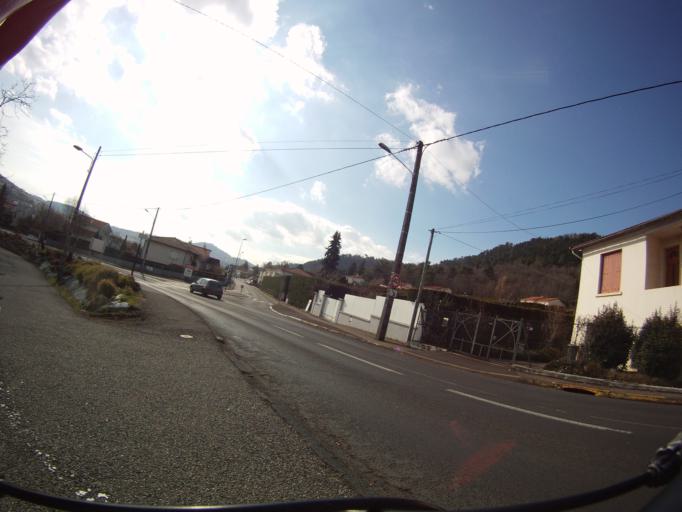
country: FR
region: Auvergne
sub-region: Departement du Puy-de-Dome
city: Ceyrat
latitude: 45.7373
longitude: 3.0611
